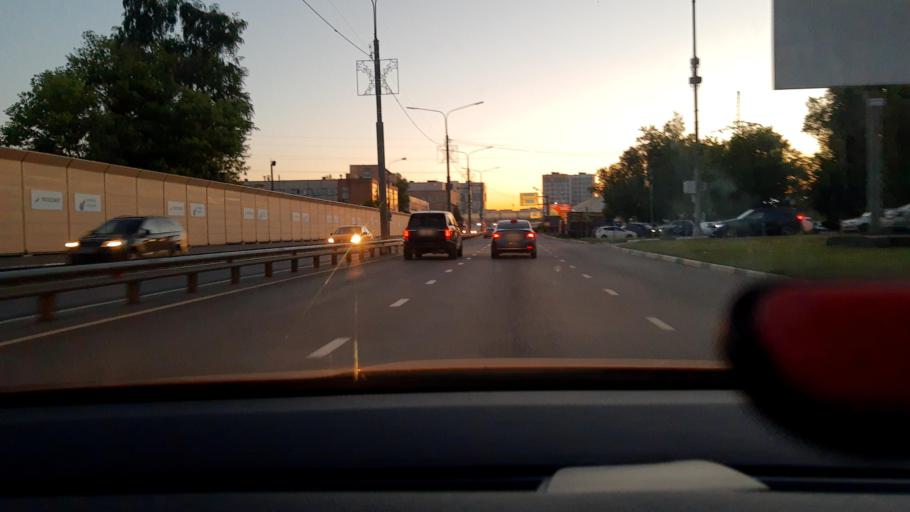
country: RU
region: Moskovskaya
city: Korolev
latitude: 55.9144
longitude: 37.7986
